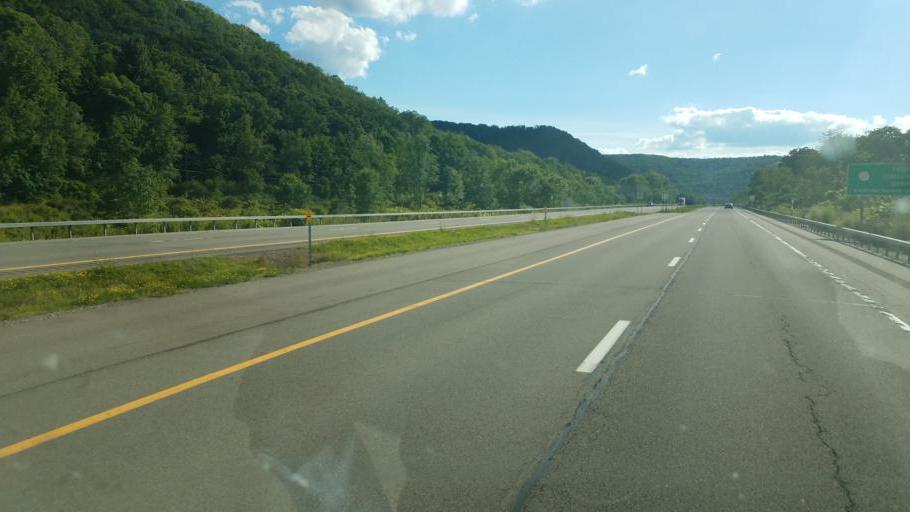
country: US
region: New York
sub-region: Cattaraugus County
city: Salamanca
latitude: 42.1062
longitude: -78.7869
